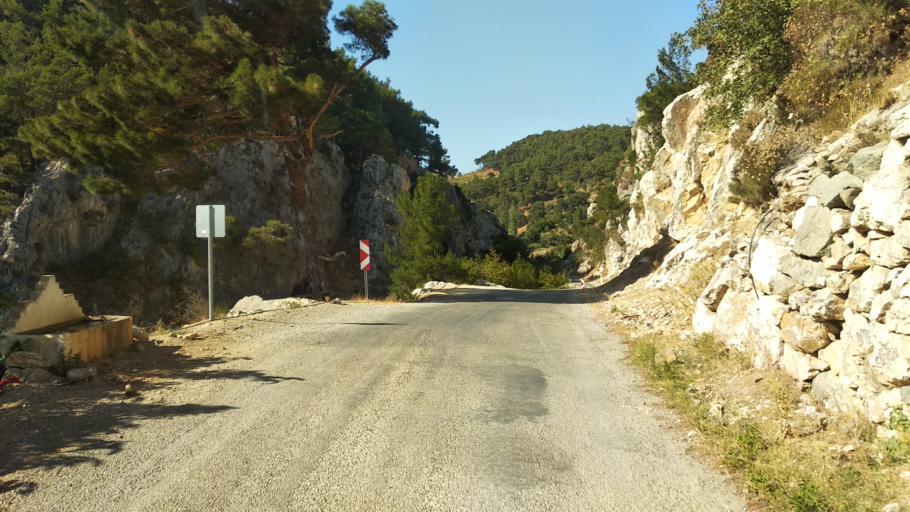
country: TR
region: Izmir
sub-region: Seferihisar
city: Seferhisar
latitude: 38.3208
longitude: 26.9571
